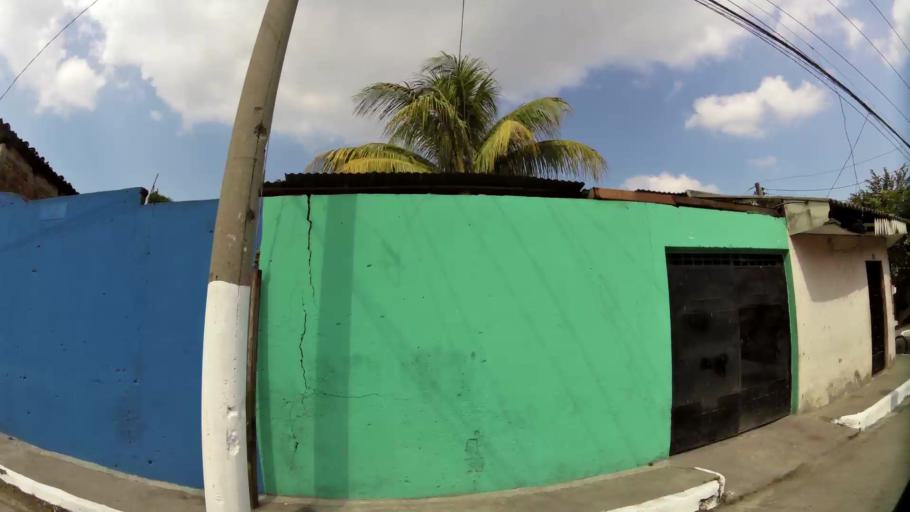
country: SV
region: San Salvador
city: Delgado
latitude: 13.7159
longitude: -89.1666
